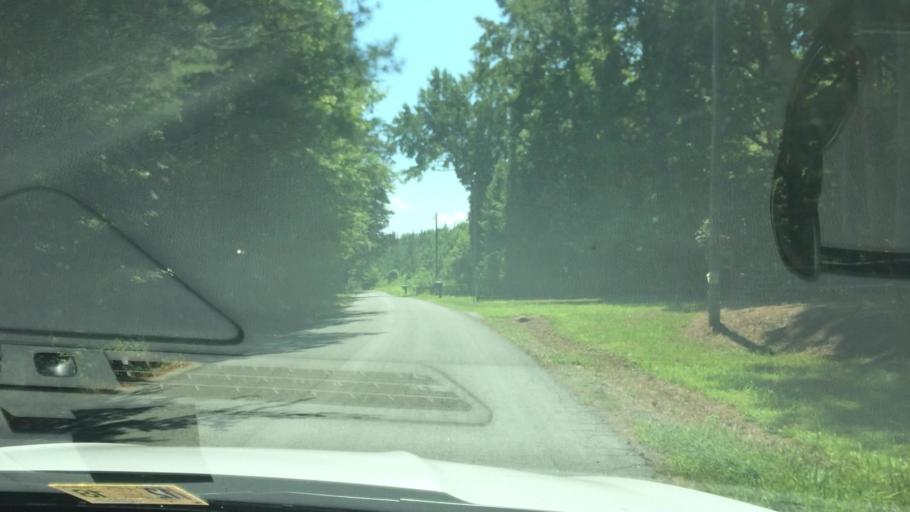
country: US
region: Virginia
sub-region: Charles City County
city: Charles City
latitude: 37.2882
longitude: -76.9650
